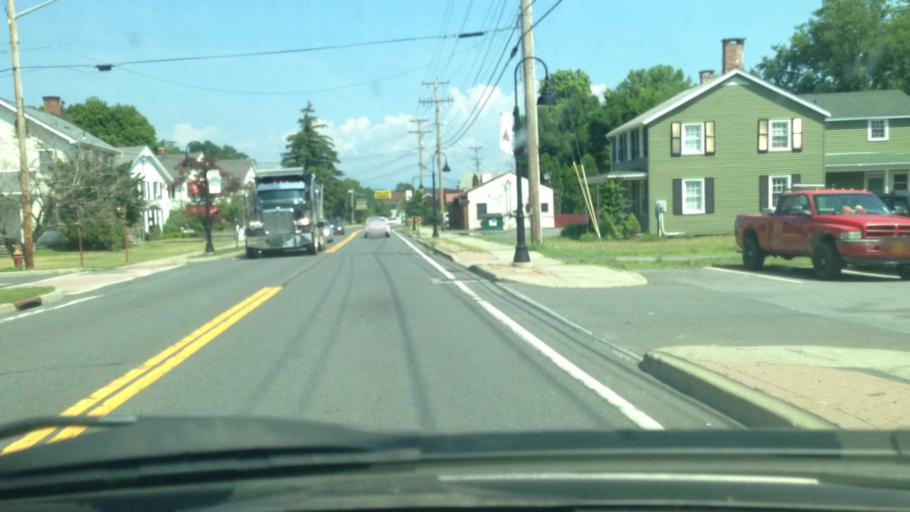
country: US
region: New York
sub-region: Ulster County
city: Port Ewen
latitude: 41.9084
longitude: -73.9771
